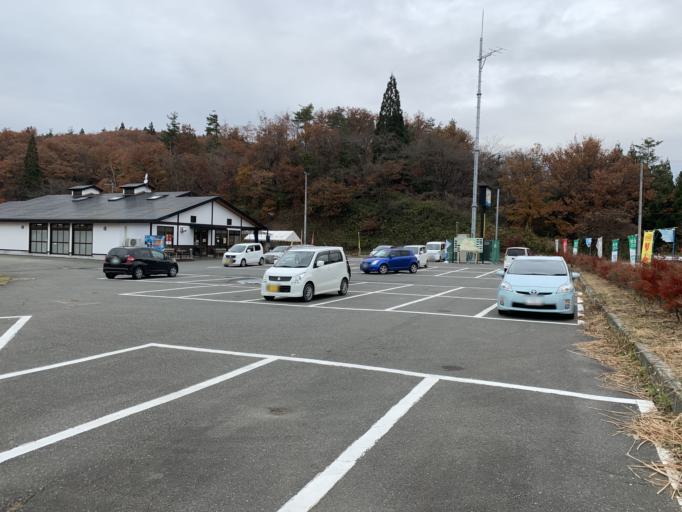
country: JP
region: Iwate
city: Kitakami
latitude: 39.2988
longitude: 141.2059
